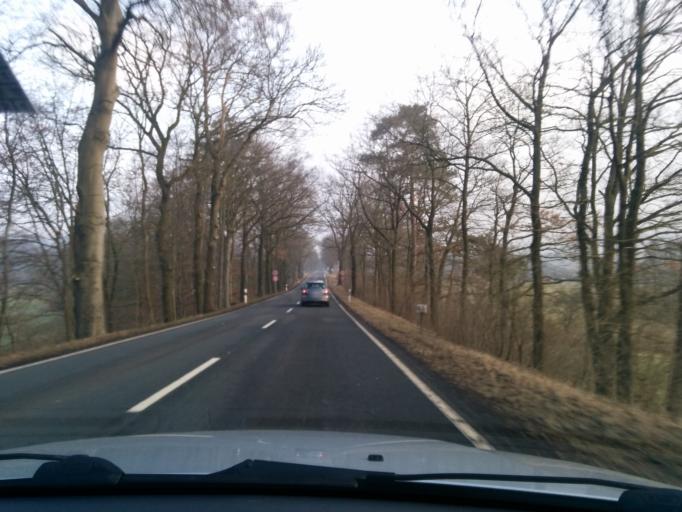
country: DE
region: Thuringia
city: Ifta
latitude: 51.0813
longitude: 10.1424
